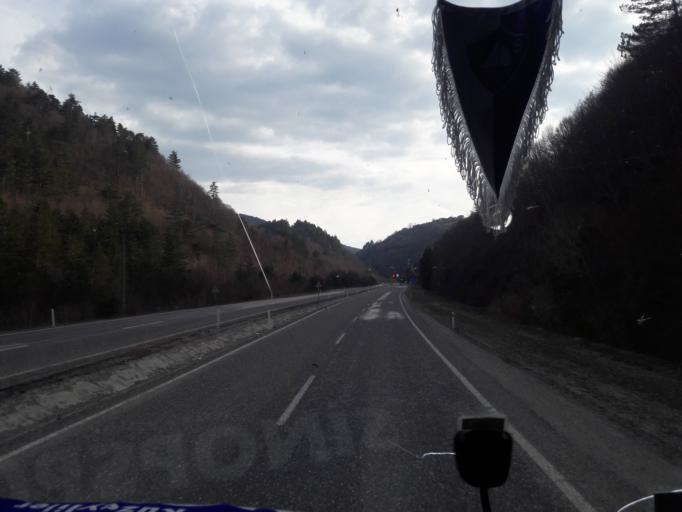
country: TR
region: Kastamonu
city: Kuzyaka
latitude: 41.1483
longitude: 33.7832
